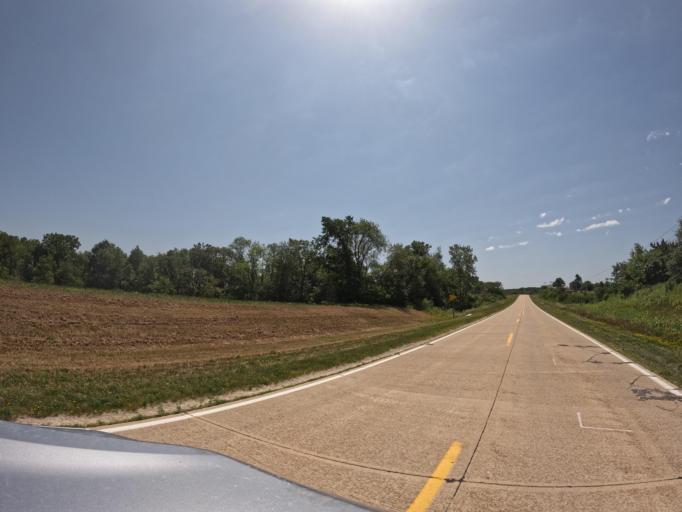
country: US
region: Iowa
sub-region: Henry County
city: Mount Pleasant
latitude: 40.9234
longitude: -91.5542
